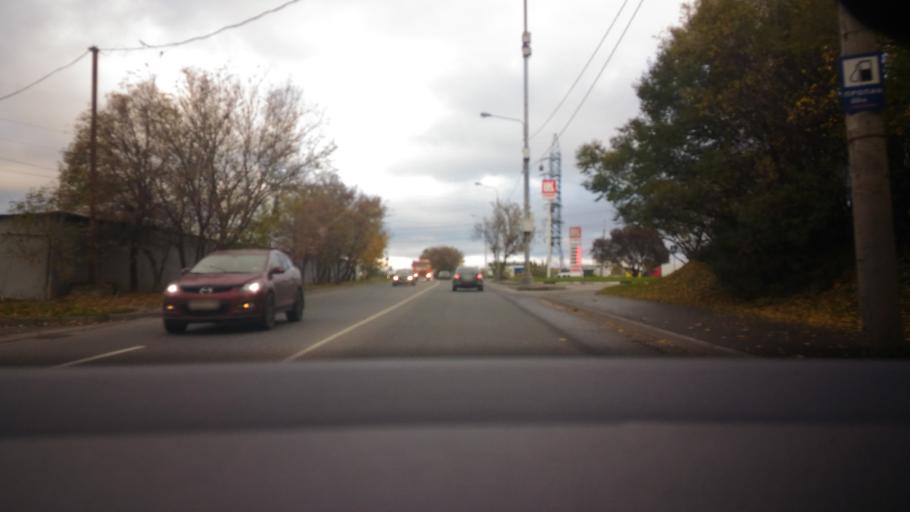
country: RU
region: Moscow
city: Strogino
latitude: 55.8345
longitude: 37.3988
